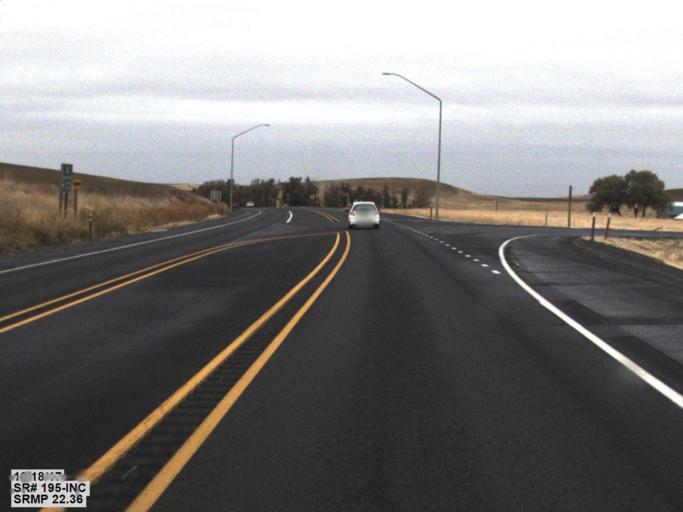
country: US
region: Washington
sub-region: Whitman County
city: Pullman
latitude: 46.7360
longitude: -117.2255
